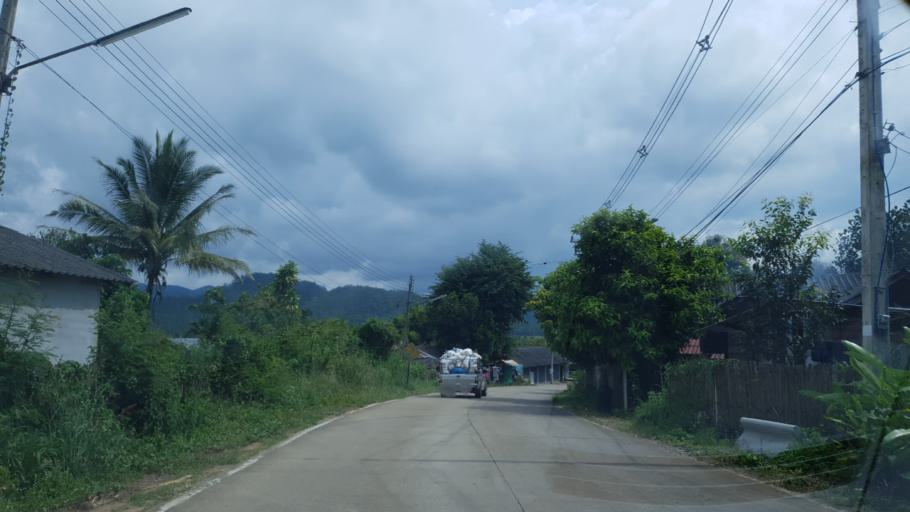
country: TH
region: Mae Hong Son
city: Khun Yuam
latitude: 18.8185
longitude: 97.9316
